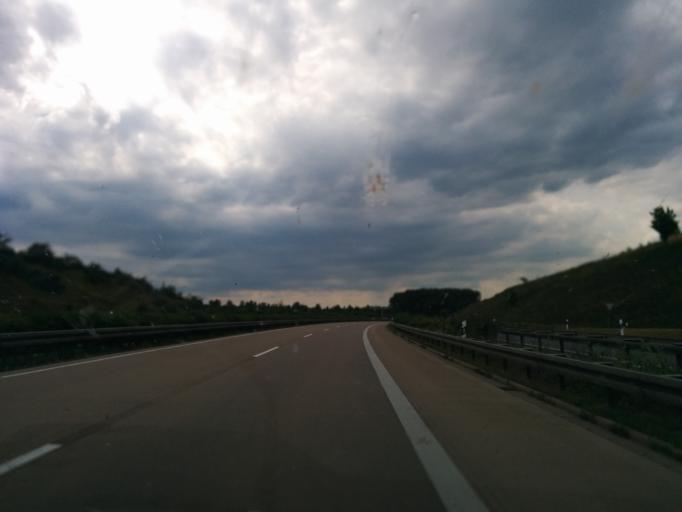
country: DE
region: Thuringia
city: Ichtershausen
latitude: 50.8950
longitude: 10.9541
